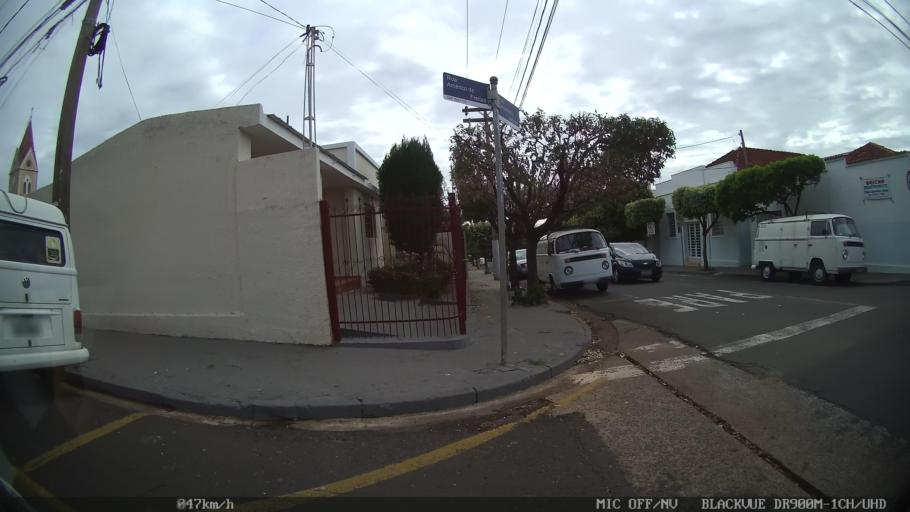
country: BR
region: Sao Paulo
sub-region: Sao Jose Do Rio Preto
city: Sao Jose do Rio Preto
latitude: -20.8152
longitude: -49.3699
